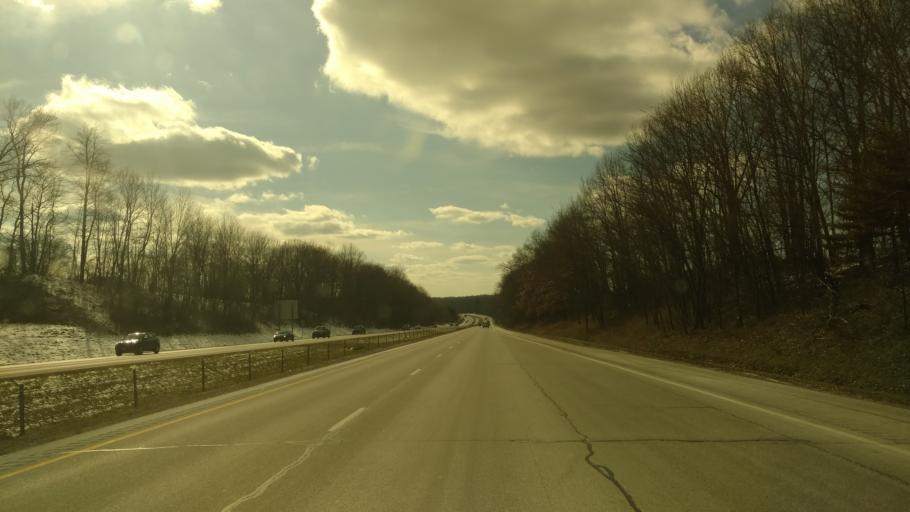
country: US
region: Ohio
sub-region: Portage County
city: Brimfield
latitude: 41.1072
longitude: -81.3547
